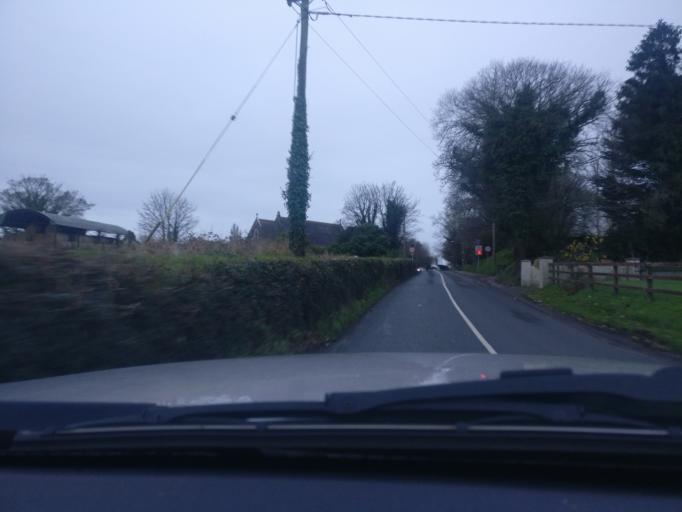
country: IE
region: Leinster
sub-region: An Mhi
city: Dunshaughlin
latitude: 53.4916
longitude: -6.6058
